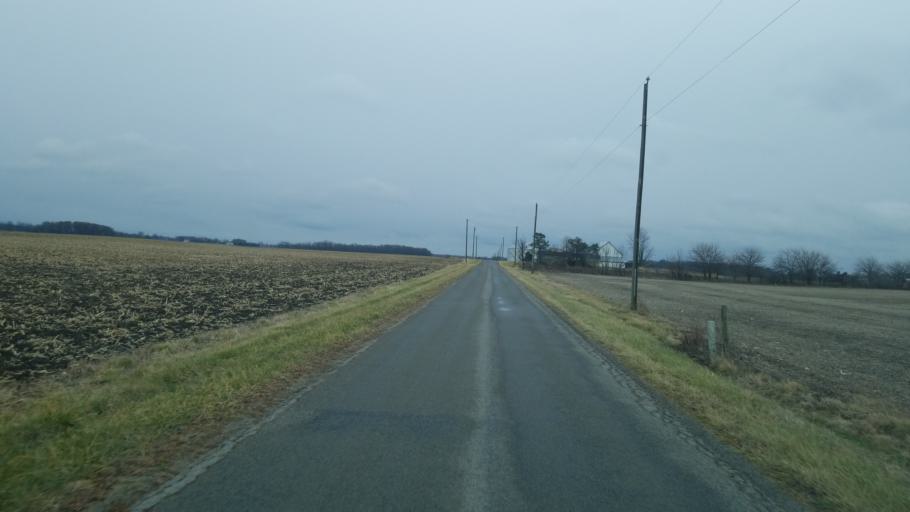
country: US
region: Ohio
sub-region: Union County
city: Marysville
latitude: 40.3105
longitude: -83.3217
